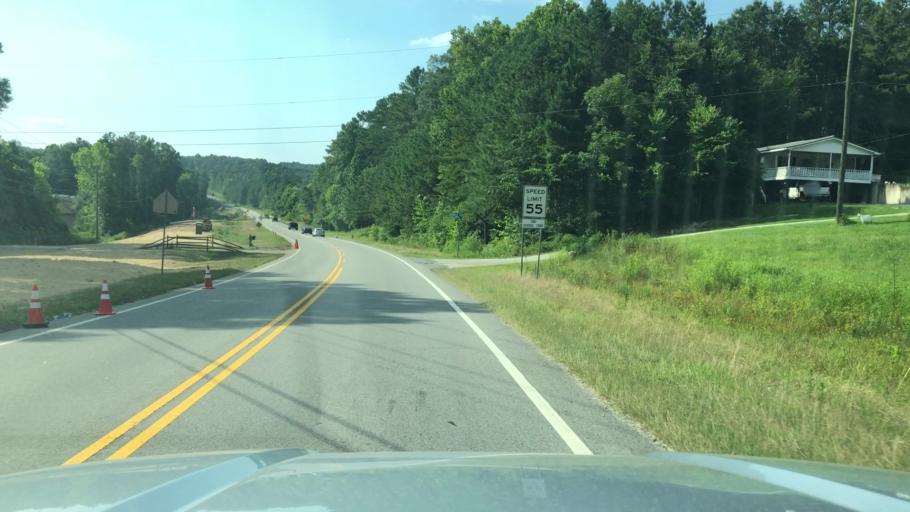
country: US
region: Georgia
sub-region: Paulding County
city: Dallas
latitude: 33.9588
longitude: -84.8519
